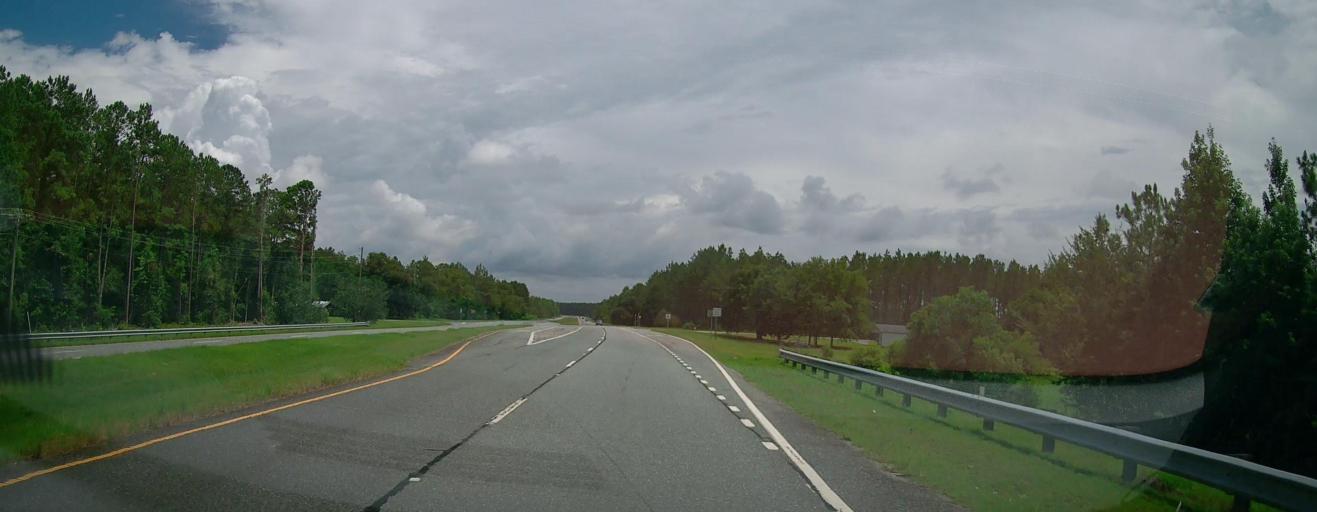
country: US
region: Georgia
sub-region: Dodge County
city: Eastman
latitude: 32.1871
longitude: -83.2015
